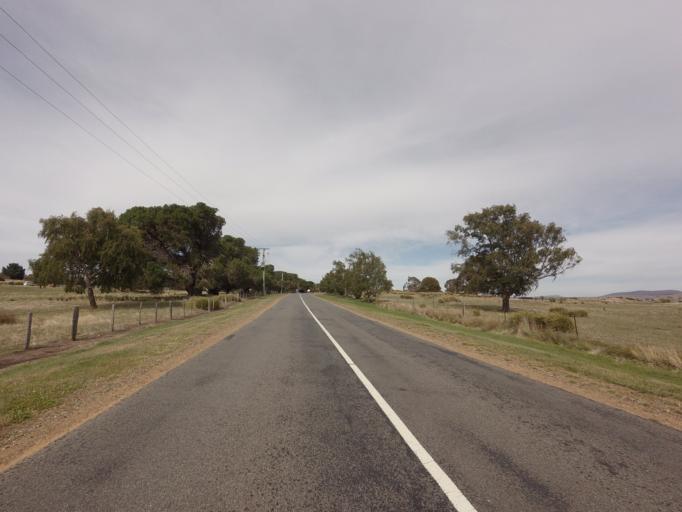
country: AU
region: Tasmania
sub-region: Brighton
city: Bridgewater
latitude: -42.2962
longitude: 147.3841
